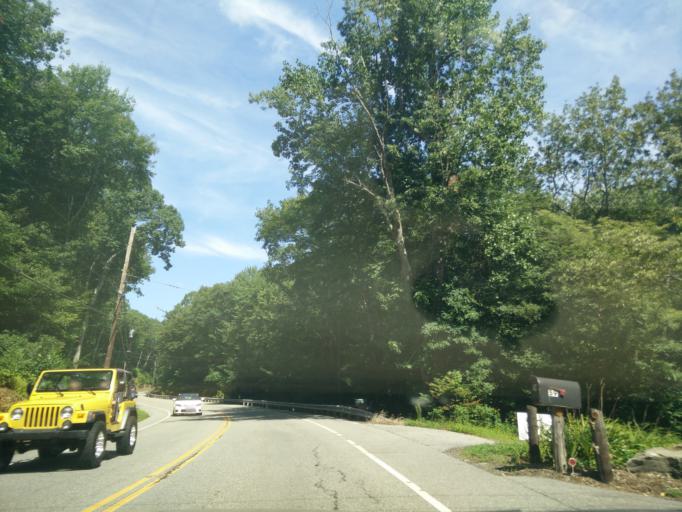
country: US
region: Connecticut
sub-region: Middlesex County
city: Clinton
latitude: 41.3345
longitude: -72.5532
